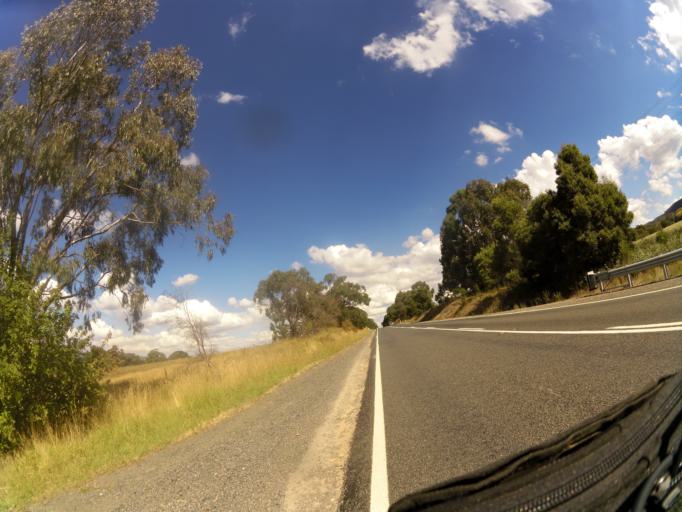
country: AU
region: Victoria
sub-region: Mansfield
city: Mansfield
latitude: -36.8848
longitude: 145.9948
